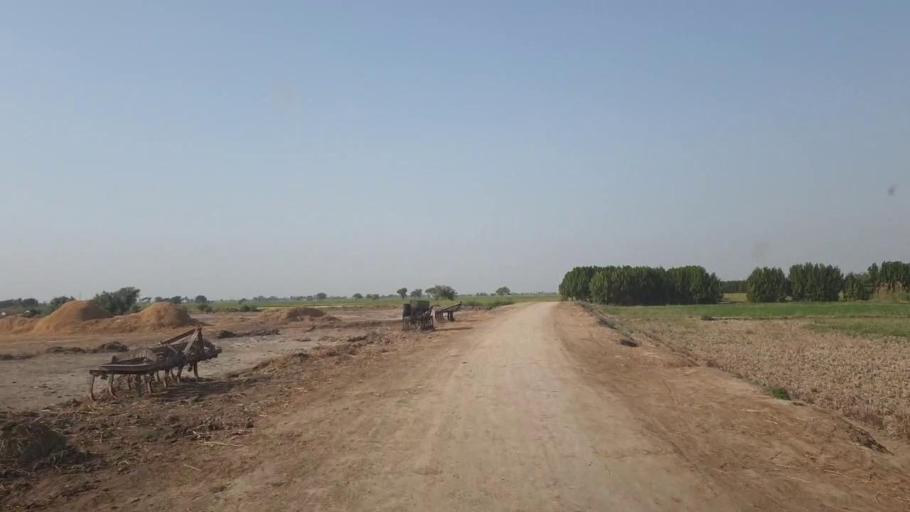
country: PK
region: Sindh
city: Kario
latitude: 24.5808
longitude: 68.5441
